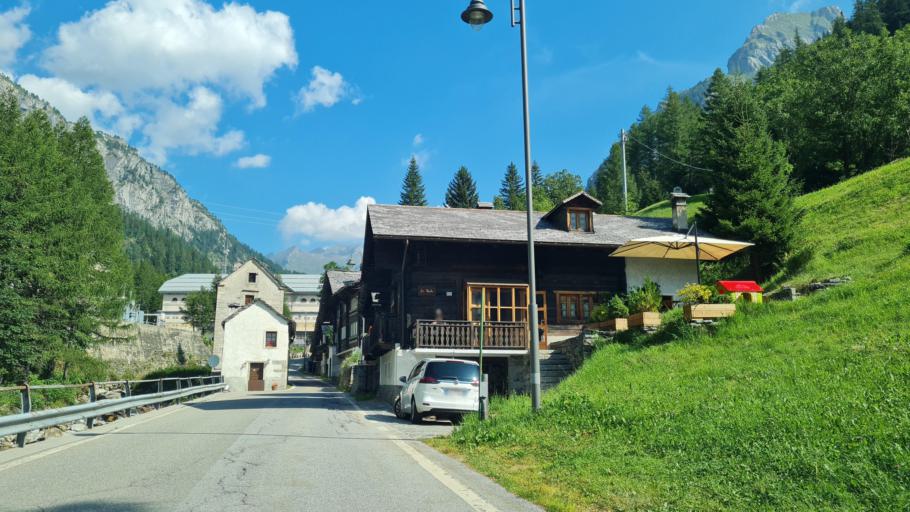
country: IT
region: Piedmont
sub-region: Provincia Verbano-Cusio-Ossola
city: Formazza
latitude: 46.3786
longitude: 8.4253
